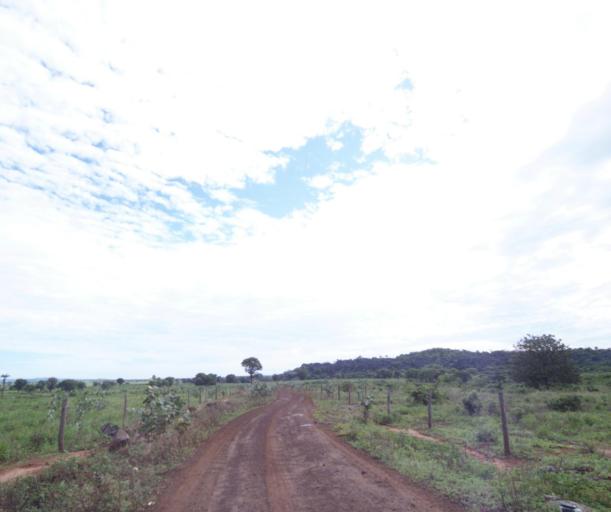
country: BR
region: Bahia
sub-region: Carinhanha
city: Carinhanha
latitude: -14.2441
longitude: -44.4173
